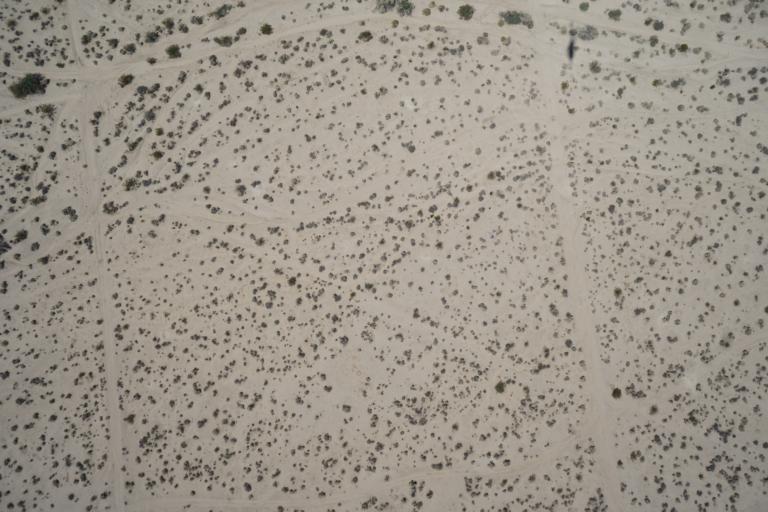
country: US
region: California
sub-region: San Bernardino County
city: Twentynine Palms
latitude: 34.1312
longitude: -116.0419
